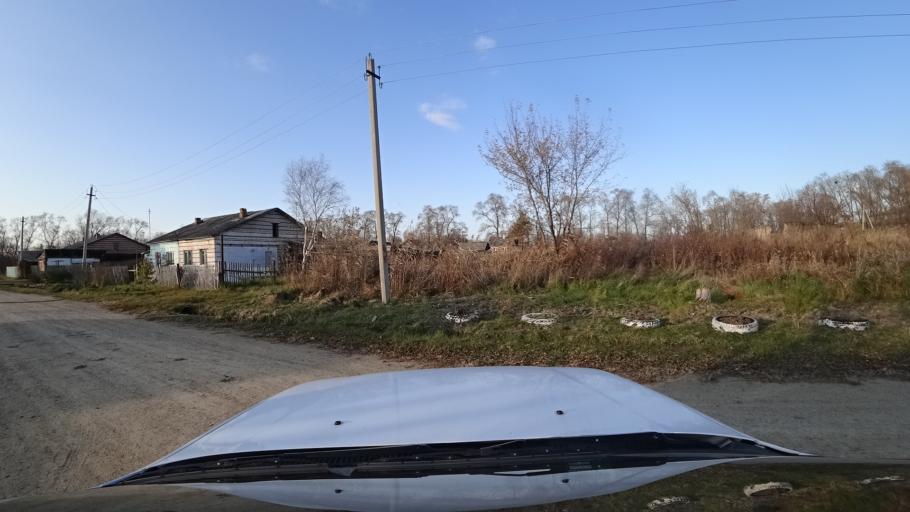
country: RU
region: Primorskiy
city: Lazo
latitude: 45.8268
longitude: 133.6160
